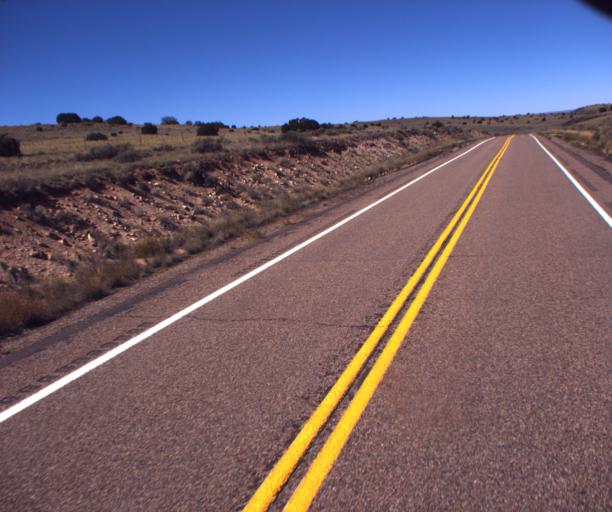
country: US
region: Arizona
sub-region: Apache County
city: Saint Johns
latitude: 34.5604
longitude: -109.5012
